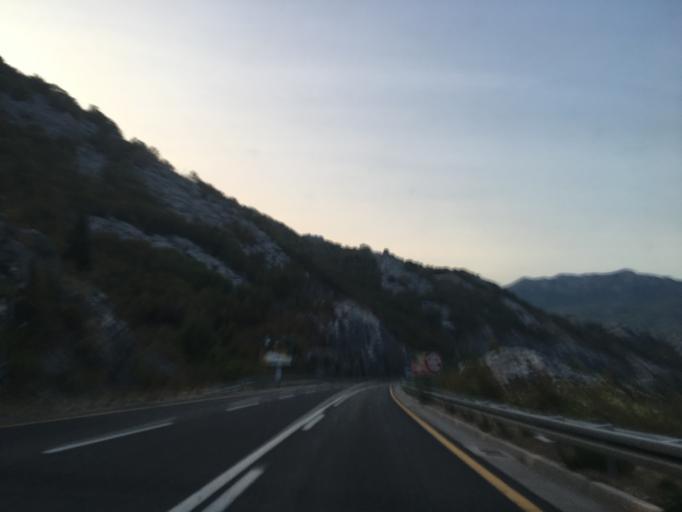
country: ME
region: Bar
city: Sutomore
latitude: 42.2091
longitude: 19.0487
